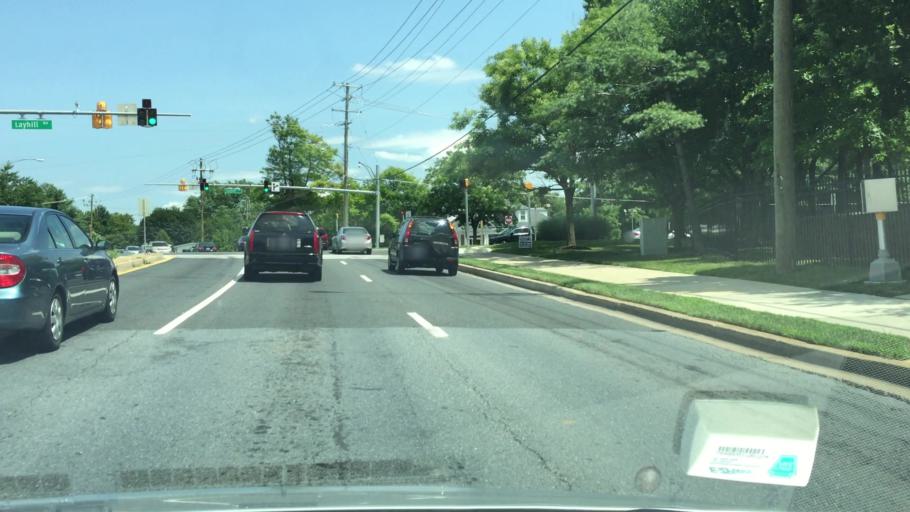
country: US
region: Maryland
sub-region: Montgomery County
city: Layhill
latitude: 39.0905
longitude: -77.0456
